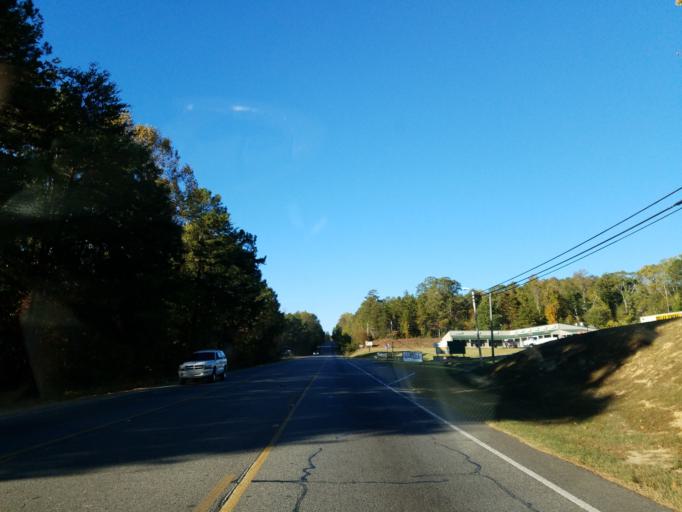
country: US
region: Georgia
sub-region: Cherokee County
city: Ball Ground
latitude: 34.3530
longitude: -84.3791
